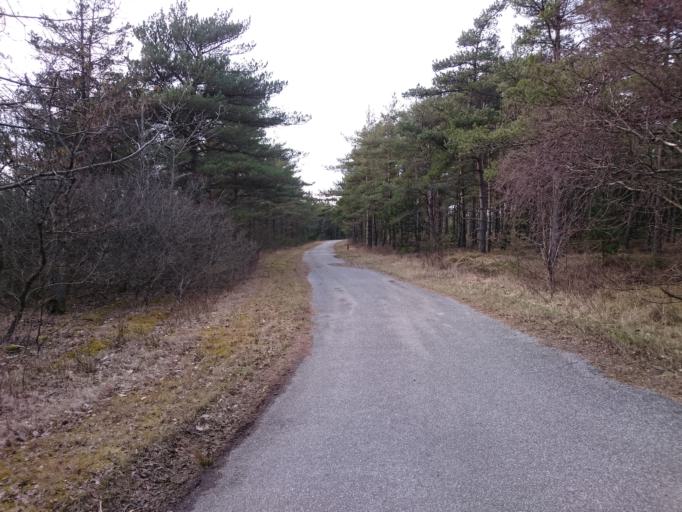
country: DK
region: North Denmark
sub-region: Frederikshavn Kommune
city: Skagen
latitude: 57.6998
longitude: 10.5186
